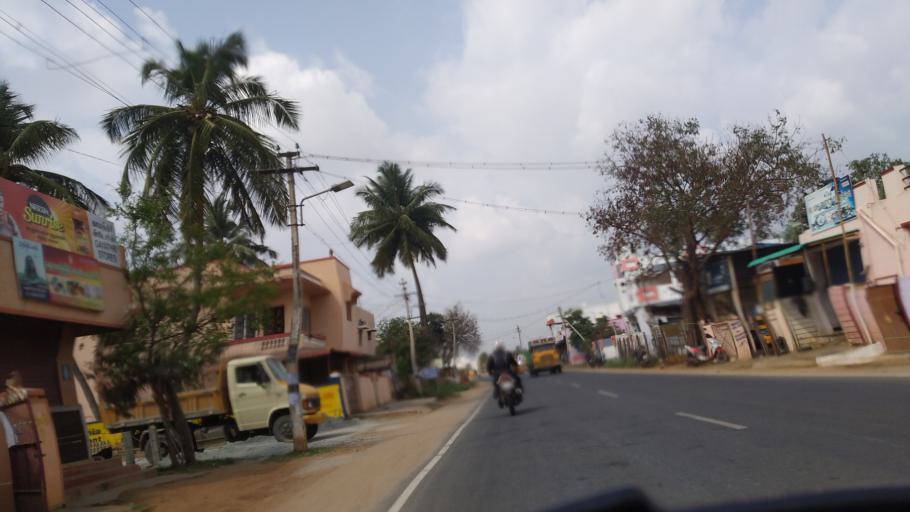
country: IN
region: Tamil Nadu
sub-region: Coimbatore
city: Perur
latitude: 10.9546
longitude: 76.9279
